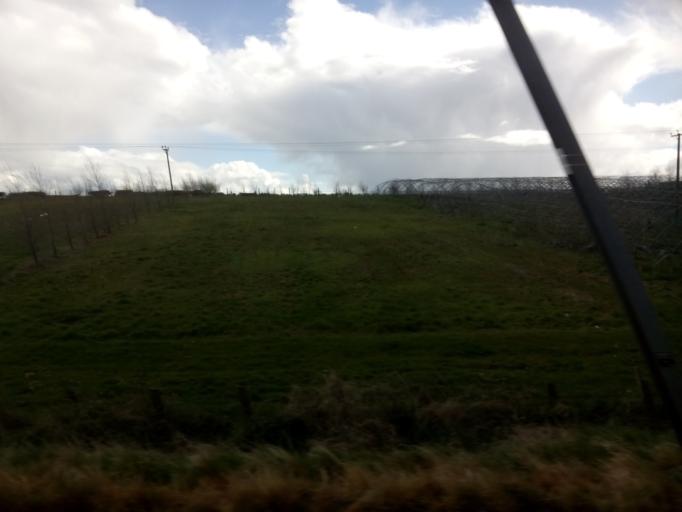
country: GB
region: Scotland
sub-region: East Lothian
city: Dunbar
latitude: 55.9906
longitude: -2.5597
